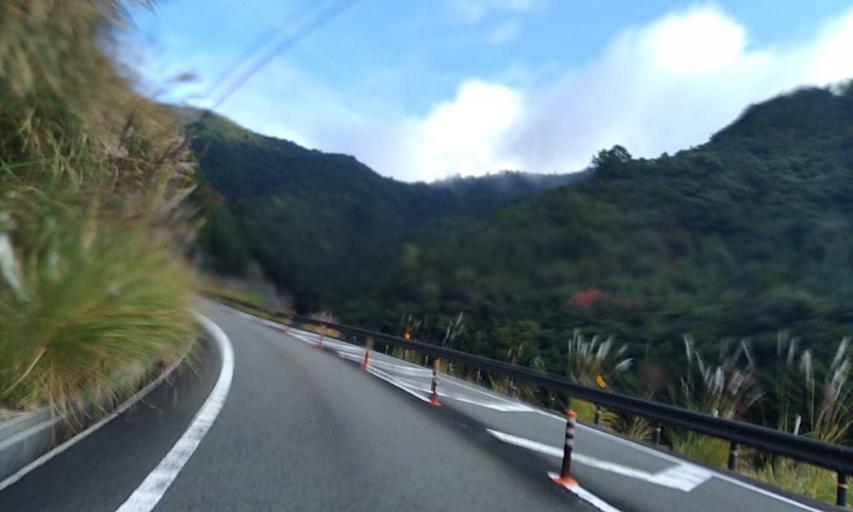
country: JP
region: Wakayama
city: Shingu
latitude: 33.8774
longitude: 135.8761
